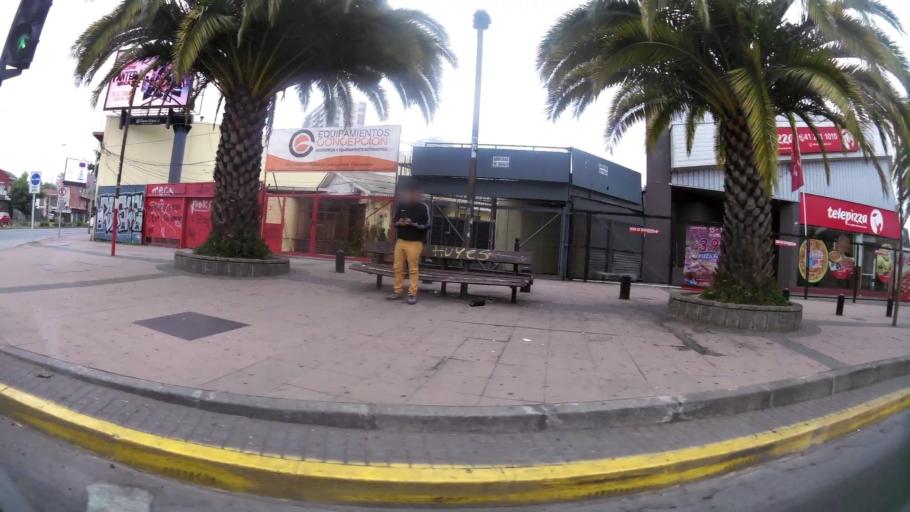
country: CL
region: Biobio
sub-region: Provincia de Concepcion
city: Concepcion
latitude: -36.8205
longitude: -73.0443
